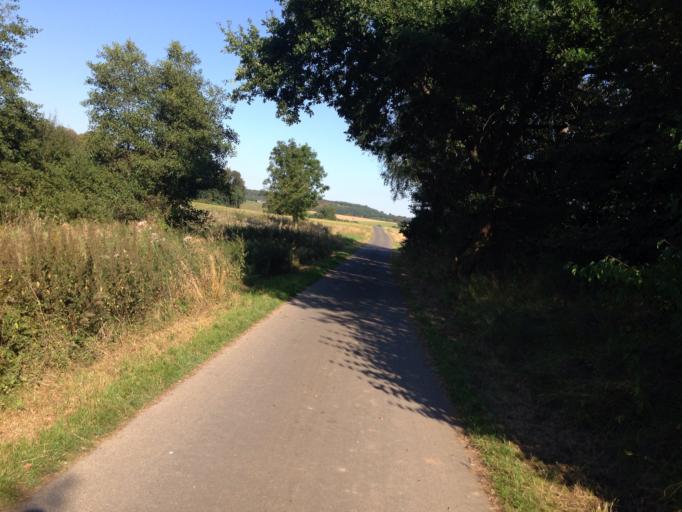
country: DE
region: Hesse
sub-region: Regierungsbezirk Giessen
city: Grunberg
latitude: 50.6403
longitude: 8.9166
